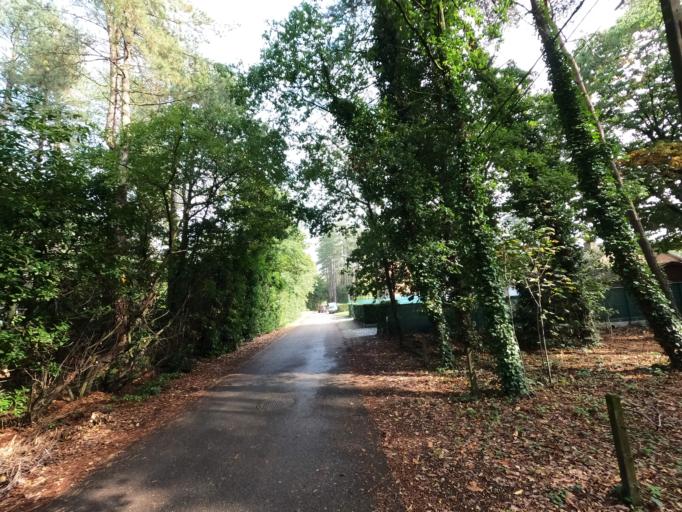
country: BE
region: Flanders
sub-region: Provincie Antwerpen
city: Kasterlee
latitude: 51.2110
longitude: 4.9082
